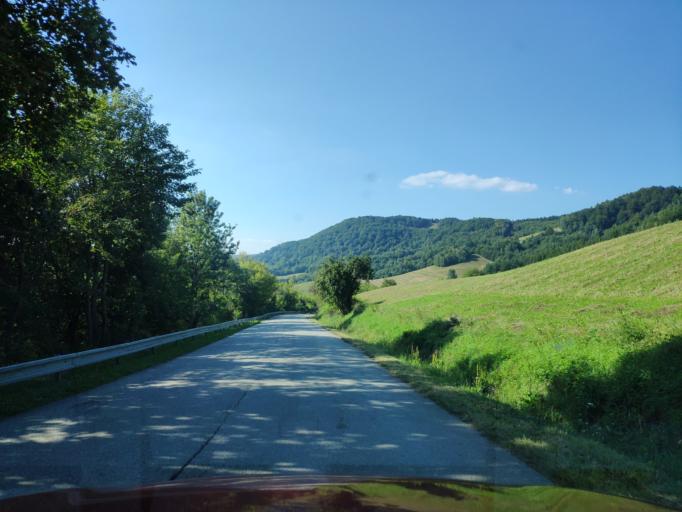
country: PL
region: Subcarpathian Voivodeship
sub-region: Powiat leski
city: Cisna
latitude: 49.0506
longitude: 22.3080
